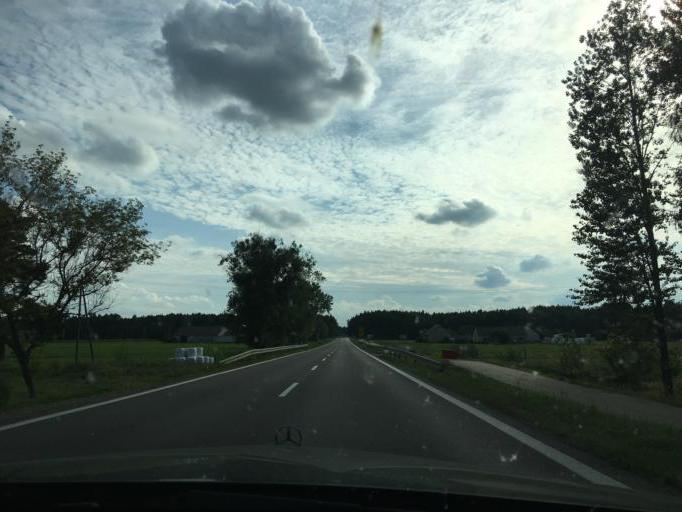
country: PL
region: Podlasie
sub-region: Powiat grajewski
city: Rajgrod
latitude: 53.7184
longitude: 22.6746
